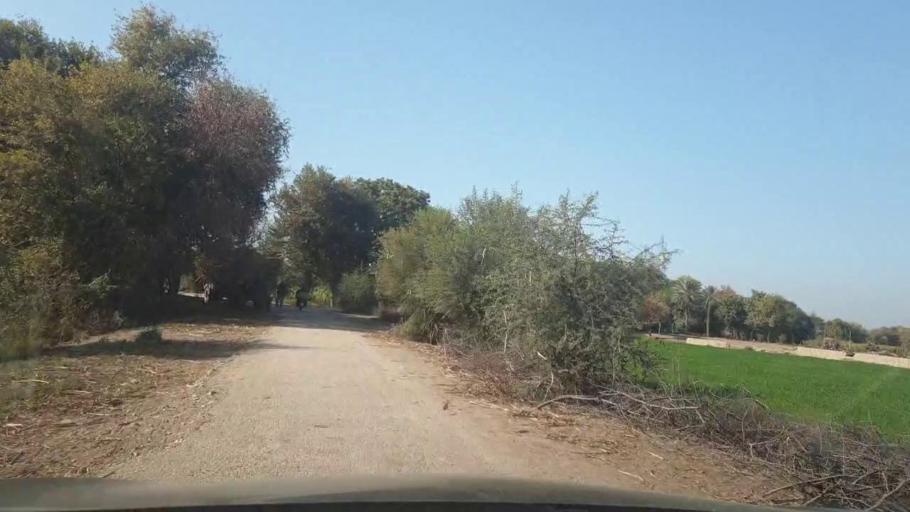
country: PK
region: Sindh
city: Khairpur
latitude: 28.1445
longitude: 69.5968
